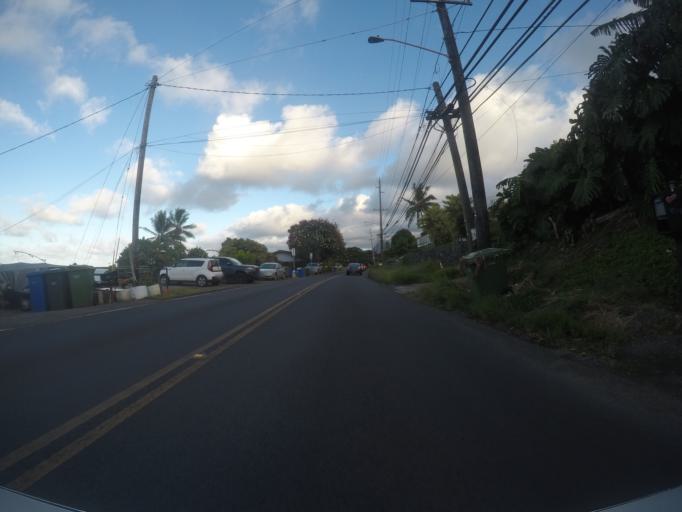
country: US
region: Hawaii
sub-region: Honolulu County
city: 'Ahuimanu
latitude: 21.4524
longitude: -157.8155
